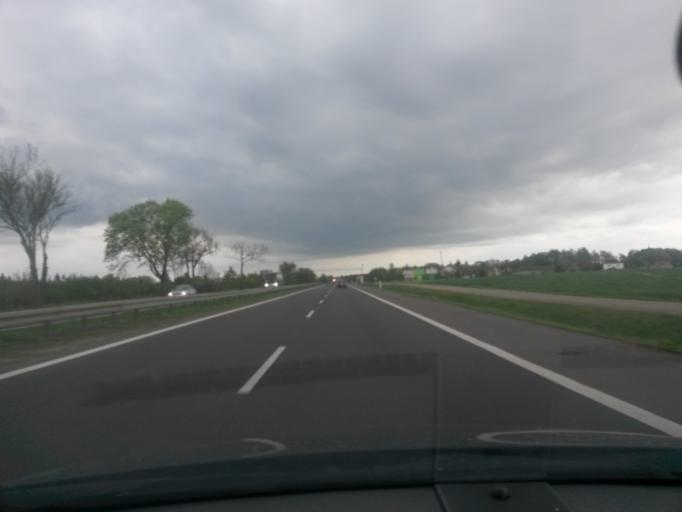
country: PL
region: Masovian Voivodeship
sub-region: Powiat plonski
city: Zaluski
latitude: 52.5718
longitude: 20.4842
